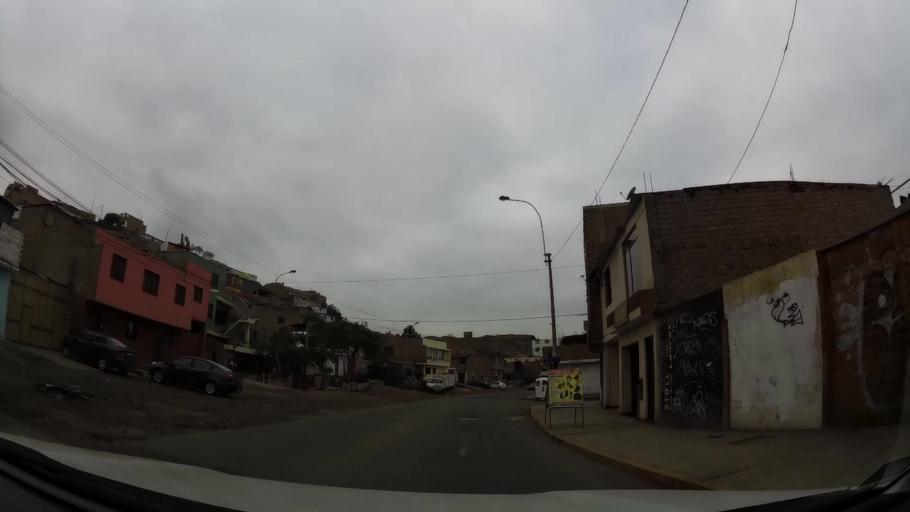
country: PE
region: Lima
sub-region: Lima
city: Surco
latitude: -12.1951
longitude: -76.9988
